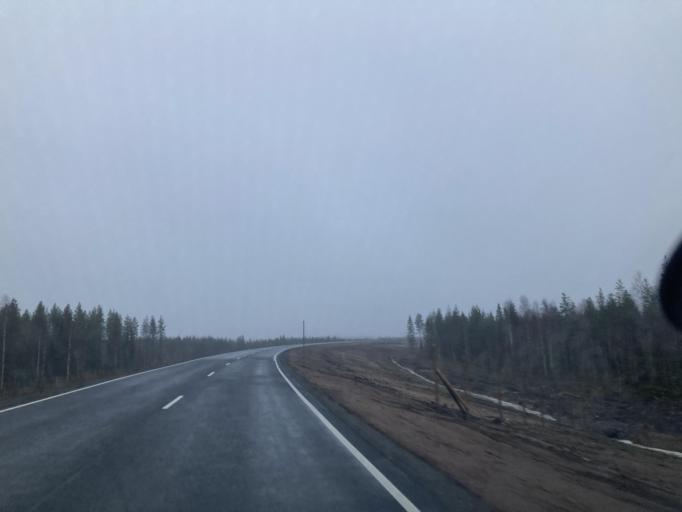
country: FI
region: Lapland
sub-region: Rovaniemi
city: Rovaniemi
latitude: 66.5897
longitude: 25.7988
